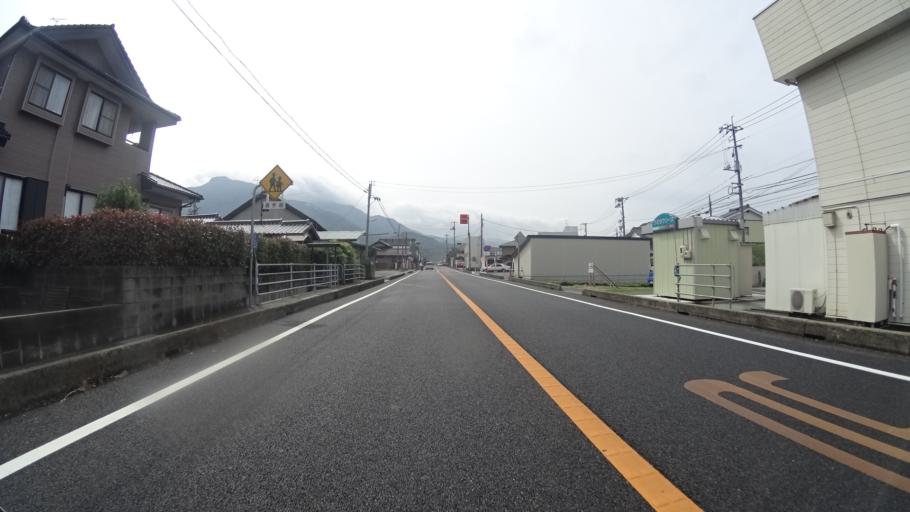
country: JP
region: Yamaguchi
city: Shimonoseki
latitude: 34.0717
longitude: 130.8993
